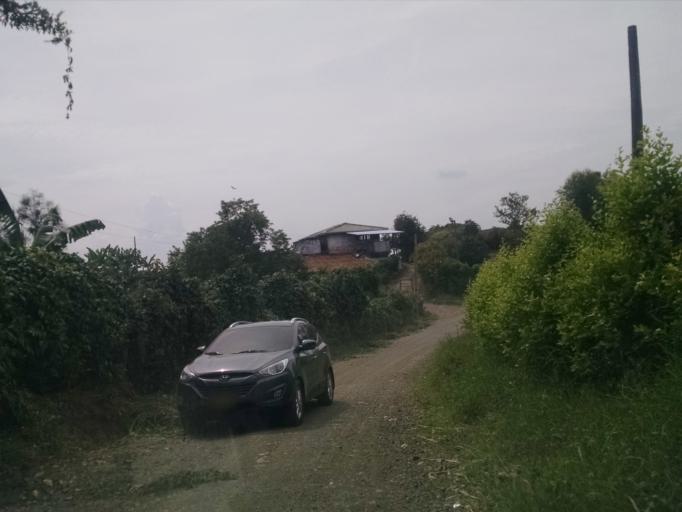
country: CO
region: Valle del Cauca
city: Ulloa
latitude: 4.7189
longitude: -75.7241
